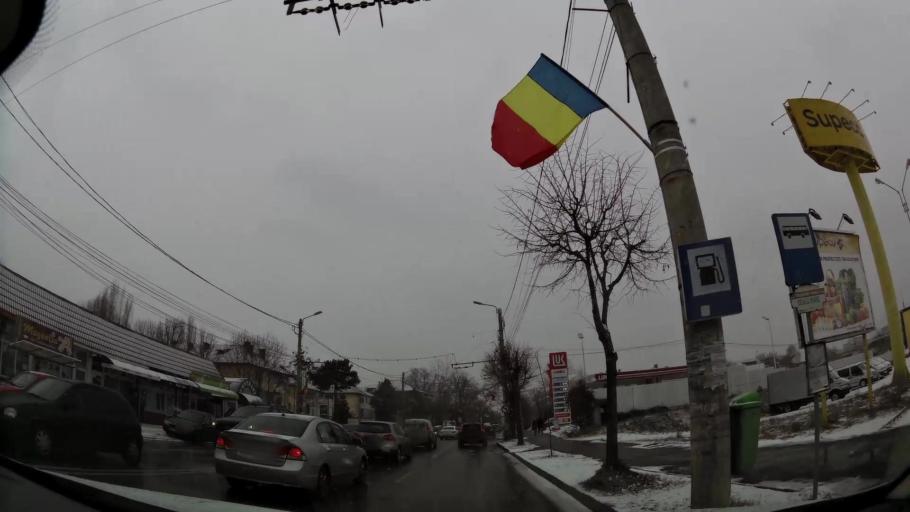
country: RO
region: Dambovita
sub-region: Municipiul Targoviste
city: Targoviste
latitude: 44.9193
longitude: 25.4596
